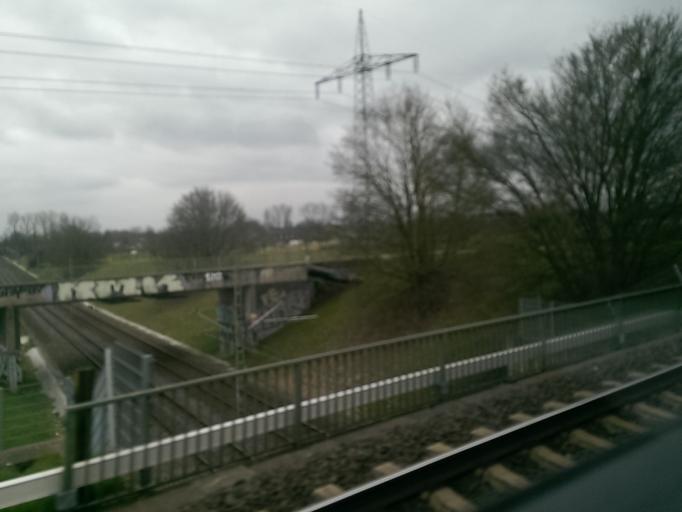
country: DE
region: North Rhine-Westphalia
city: Lanstrop
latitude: 51.5532
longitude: 7.5197
